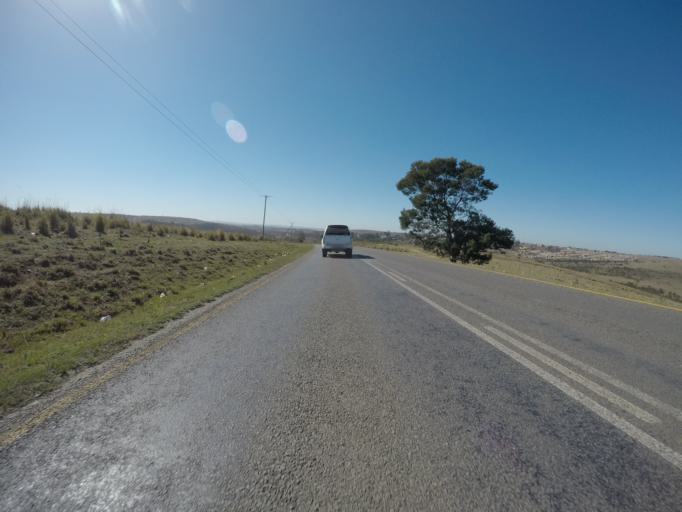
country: ZA
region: Eastern Cape
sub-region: OR Tambo District Municipality
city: Mthatha
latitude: -31.8052
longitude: 28.7545
